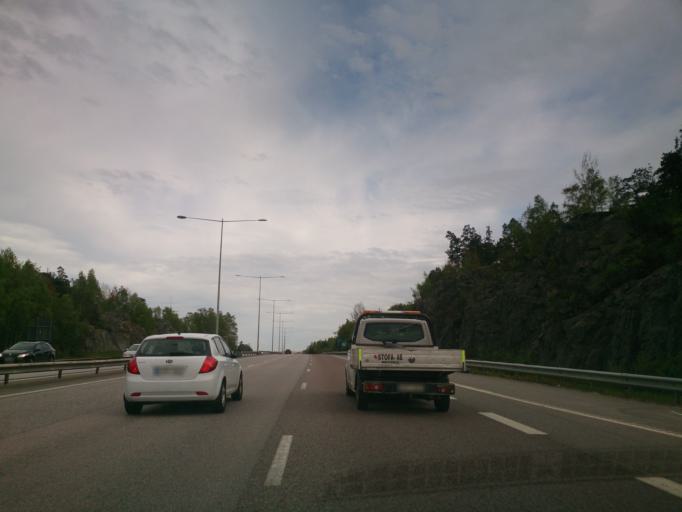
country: SE
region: Stockholm
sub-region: Haninge Kommun
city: Handen
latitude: 59.1957
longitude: 18.1360
